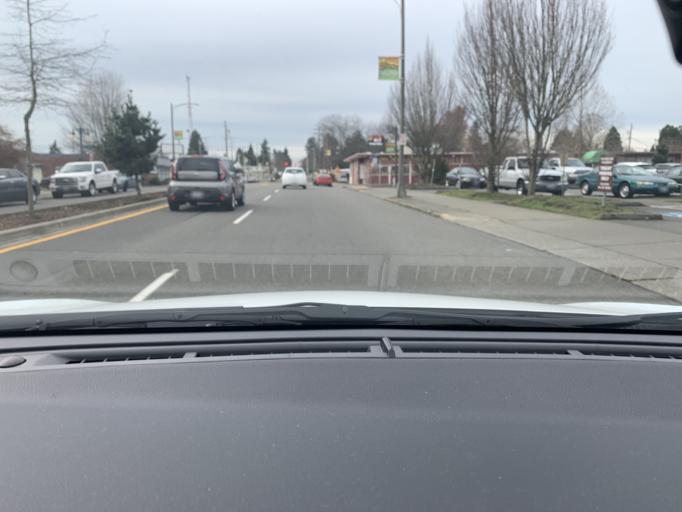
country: US
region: Washington
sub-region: Pierce County
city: Tacoma
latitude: 47.2520
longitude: -122.4526
